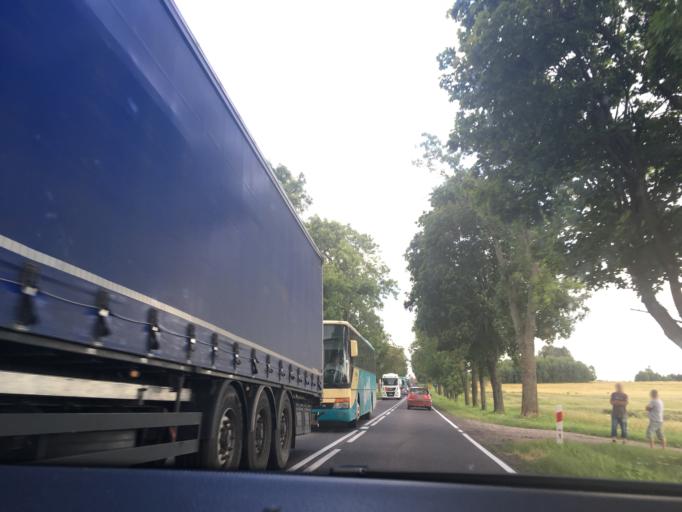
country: PL
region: Podlasie
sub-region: Powiat bielski
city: Bielsk Podlaski
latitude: 52.8167
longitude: 23.1949
